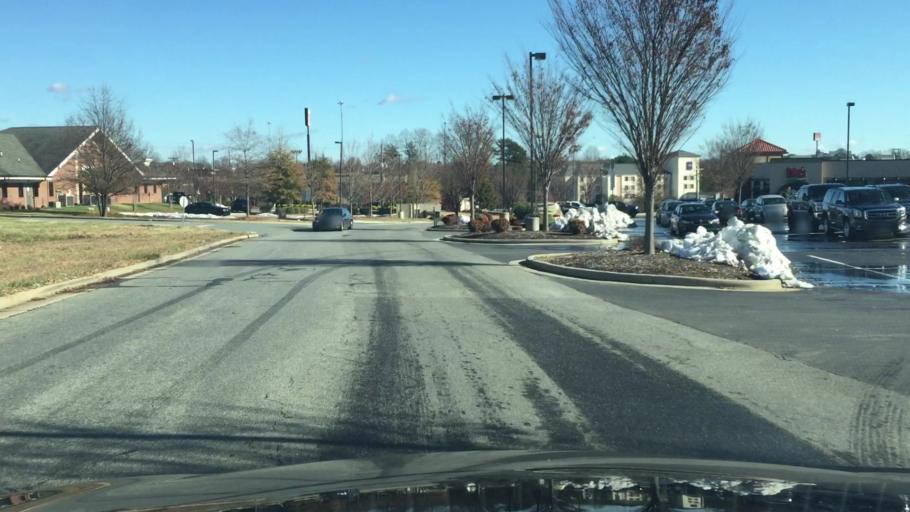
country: US
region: North Carolina
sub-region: Iredell County
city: Mooresville
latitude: 35.5935
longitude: -80.8643
